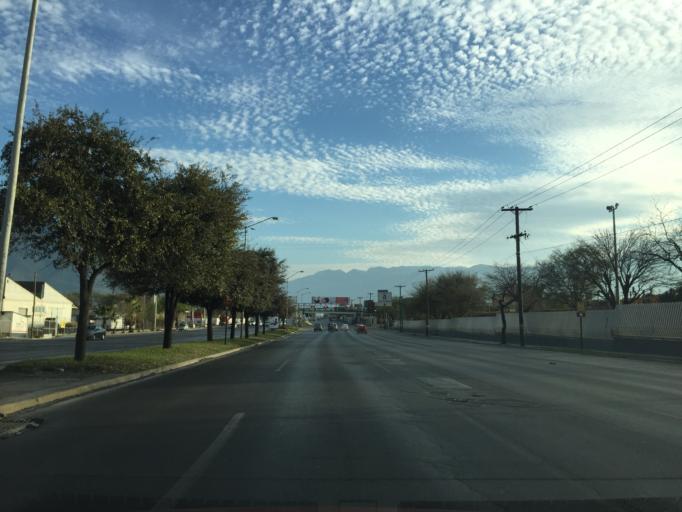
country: MX
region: Nuevo Leon
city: Guadalupe
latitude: 25.6972
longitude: -100.2683
